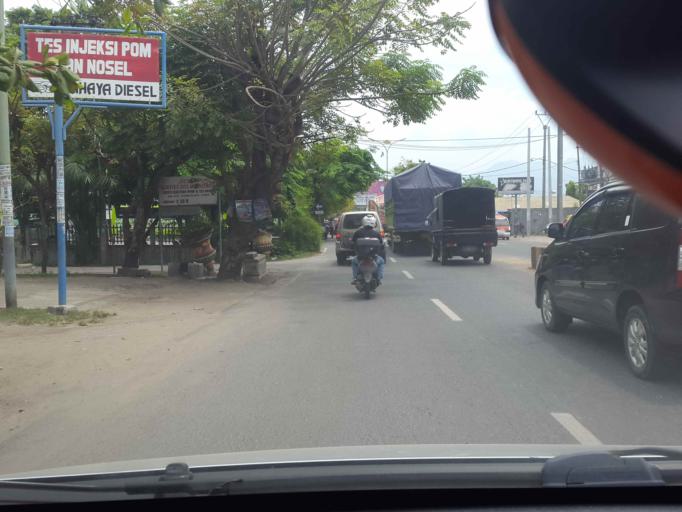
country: ID
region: Lampung
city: Bandarlampung
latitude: -5.4435
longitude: 105.2870
